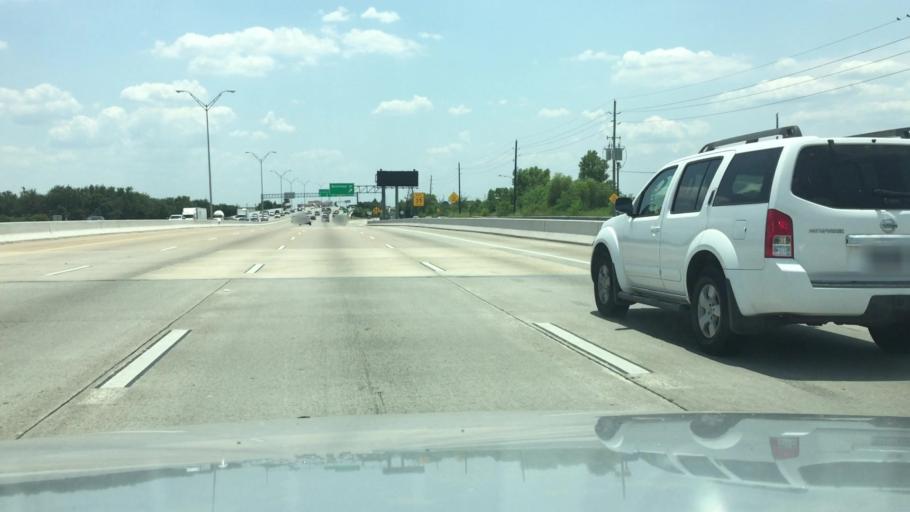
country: US
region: Texas
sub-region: Fort Bend County
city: Meadows Place
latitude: 29.6958
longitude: -95.5572
